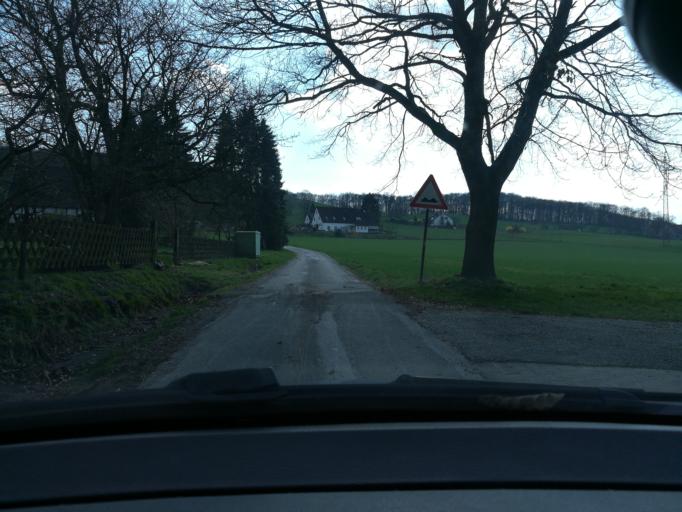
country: DE
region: North Rhine-Westphalia
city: Borgholzhausen
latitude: 52.0991
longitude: 8.3238
